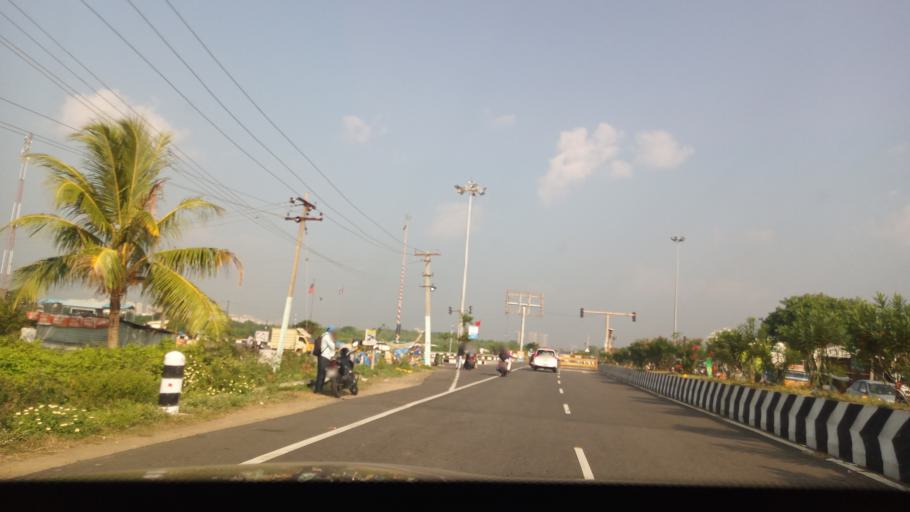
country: IN
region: Tamil Nadu
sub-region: Kancheepuram
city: Injambakkam
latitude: 12.7837
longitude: 80.2455
